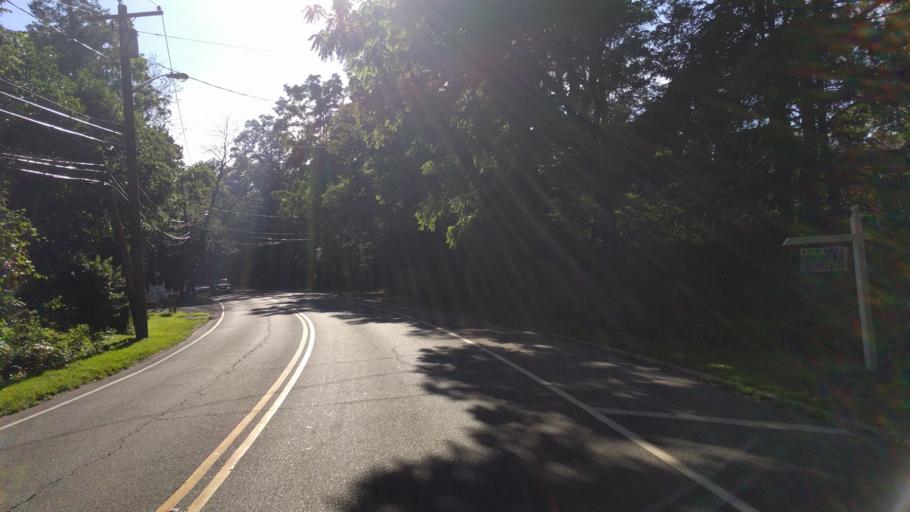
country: US
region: New York
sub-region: Nassau County
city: Oyster Bay Cove
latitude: 40.8723
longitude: -73.5143
